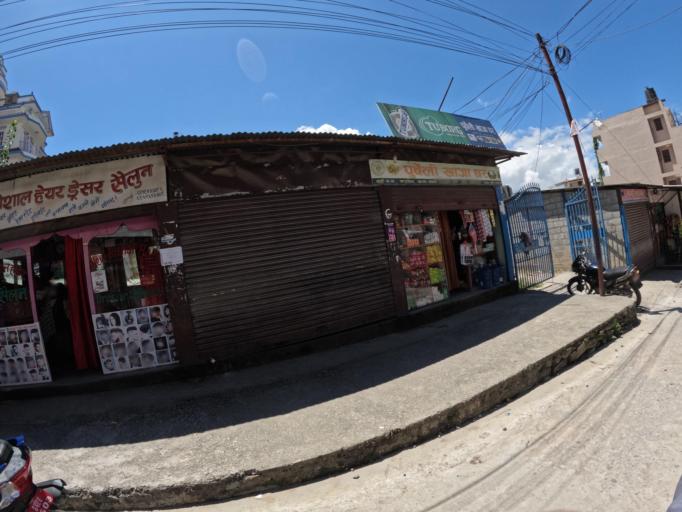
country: NP
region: Central Region
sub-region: Bagmati Zone
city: Kathmandu
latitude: 27.7508
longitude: 85.3287
